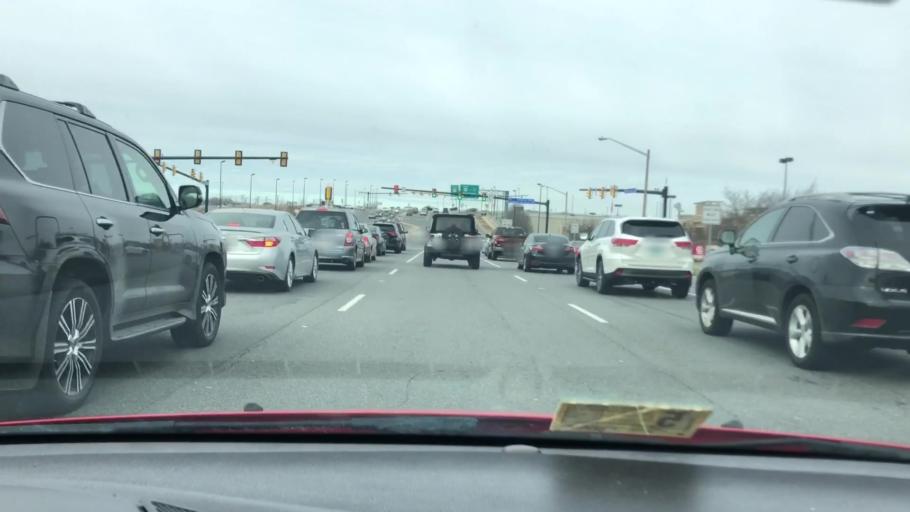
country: US
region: Virginia
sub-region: Prince William County
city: Gainesville
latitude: 38.7935
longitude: -77.6103
